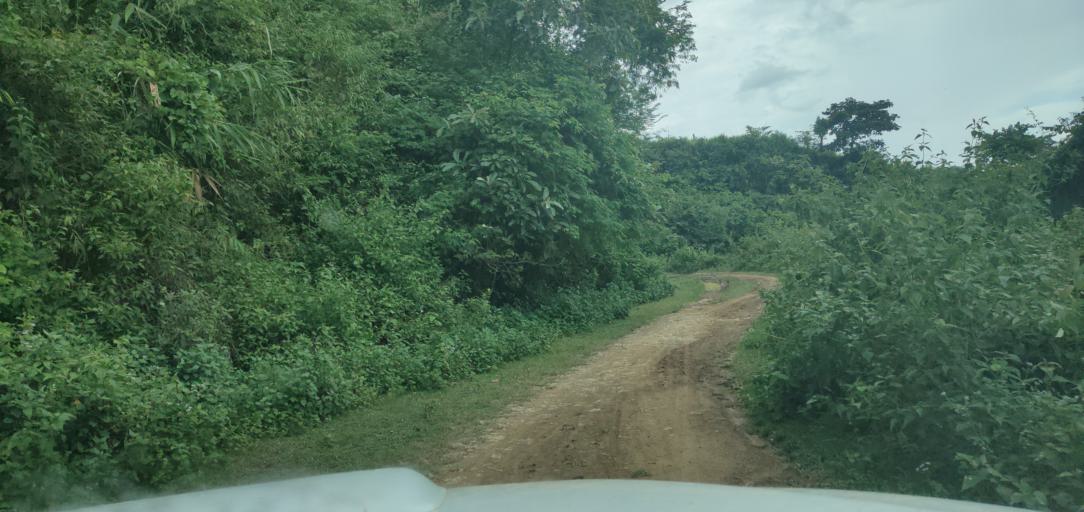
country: LA
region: Phongsali
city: Phongsali
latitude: 21.4451
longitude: 102.3157
